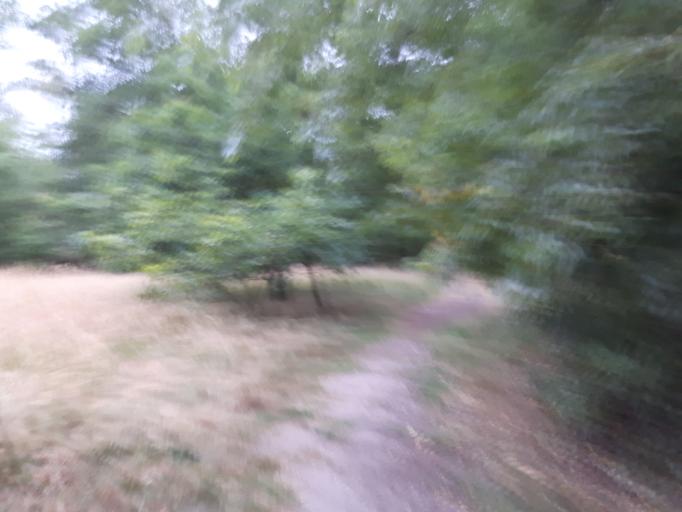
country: DE
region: Lower Saxony
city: Delmenhorst
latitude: 53.0153
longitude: 8.6850
